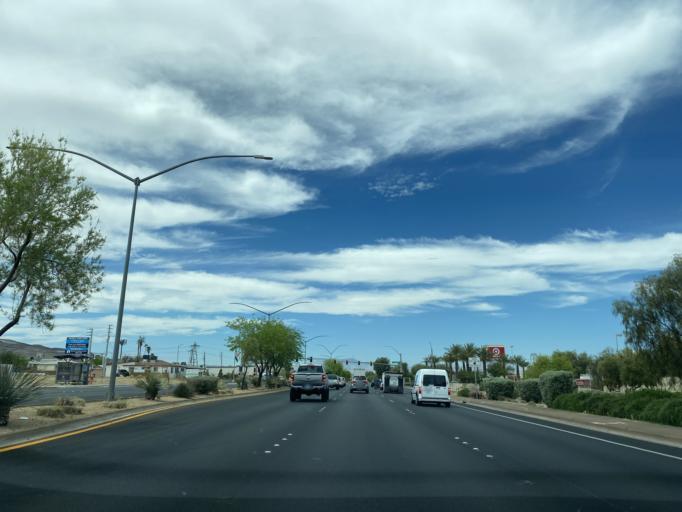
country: US
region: Nevada
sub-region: Clark County
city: Henderson
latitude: 36.0363
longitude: -114.9935
